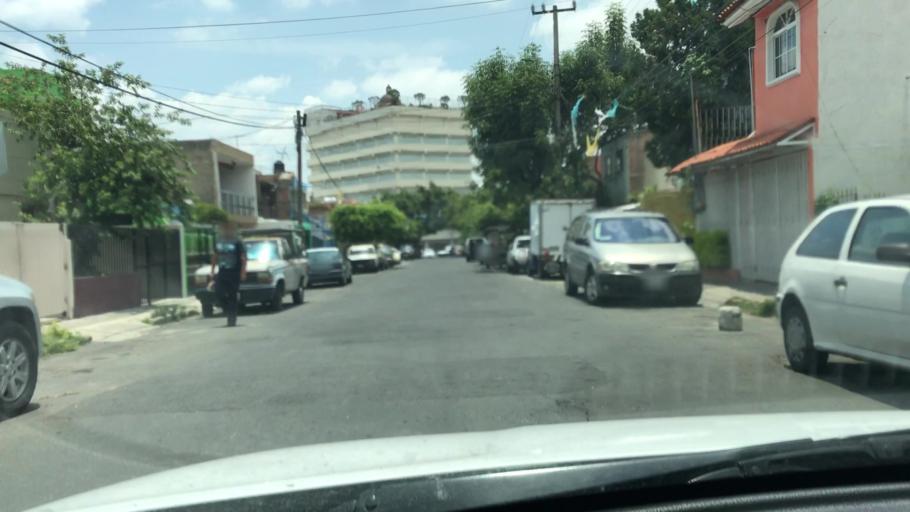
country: MX
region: Jalisco
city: Zapopan2
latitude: 20.7305
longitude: -103.4053
